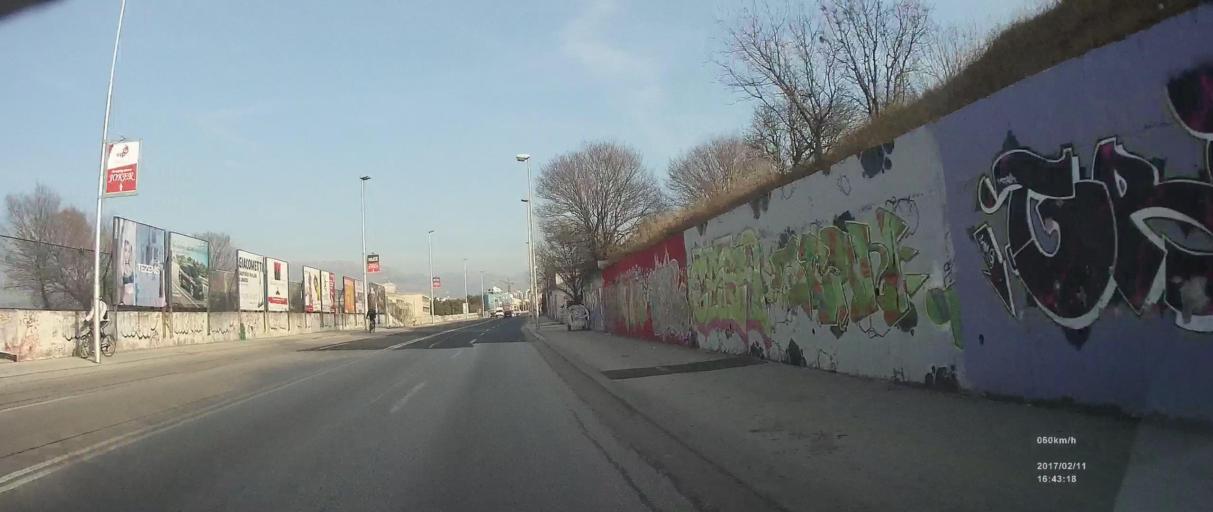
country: HR
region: Splitsko-Dalmatinska
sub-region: Grad Split
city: Split
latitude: 43.5218
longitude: 16.4396
